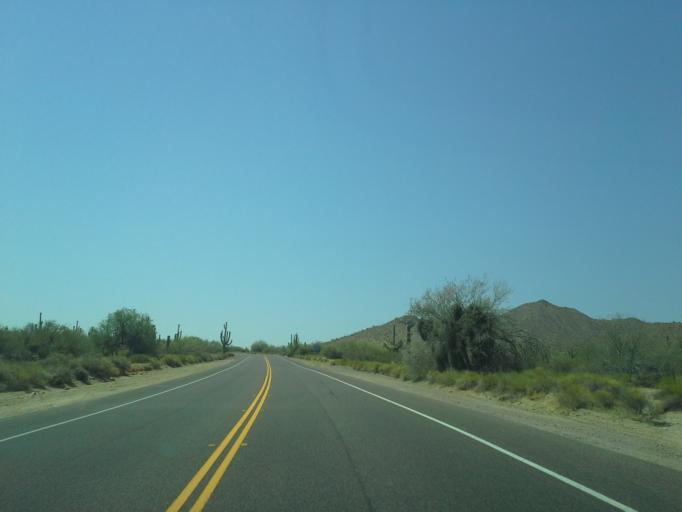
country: US
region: Arizona
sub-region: Pinal County
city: Apache Junction
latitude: 33.5166
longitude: -111.6189
